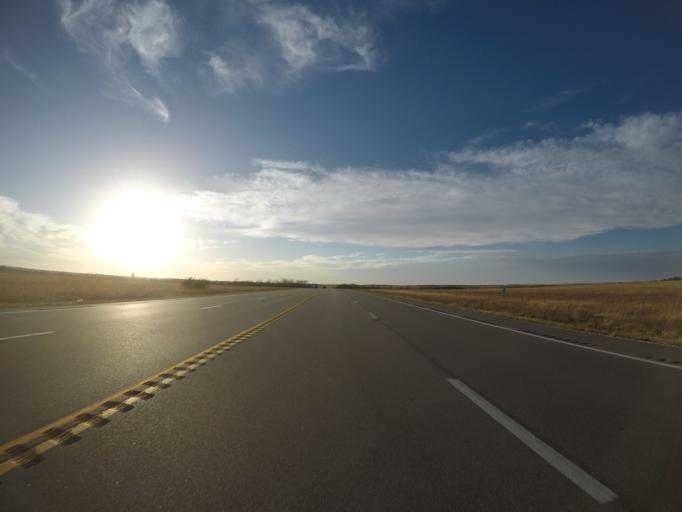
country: US
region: Kansas
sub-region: Chase County
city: Cottonwood Falls
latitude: 38.4055
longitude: -96.4148
